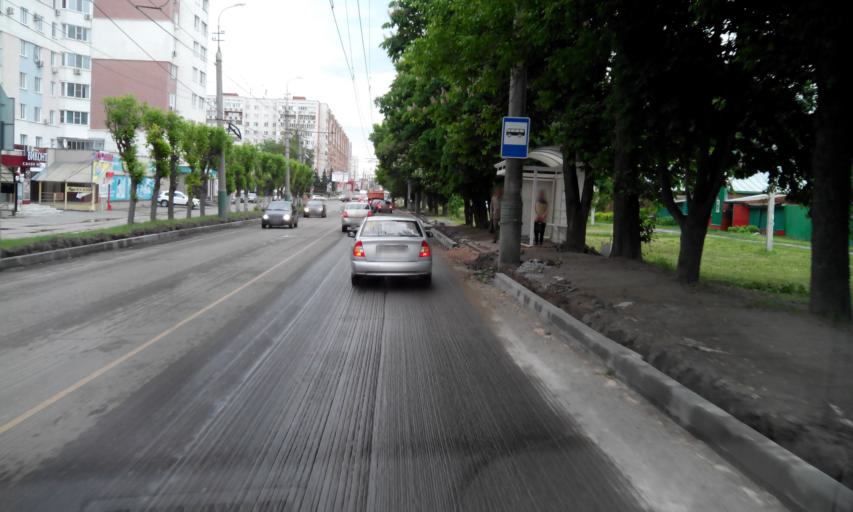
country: RU
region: Penza
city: Penza
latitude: 53.1978
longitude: 44.9953
